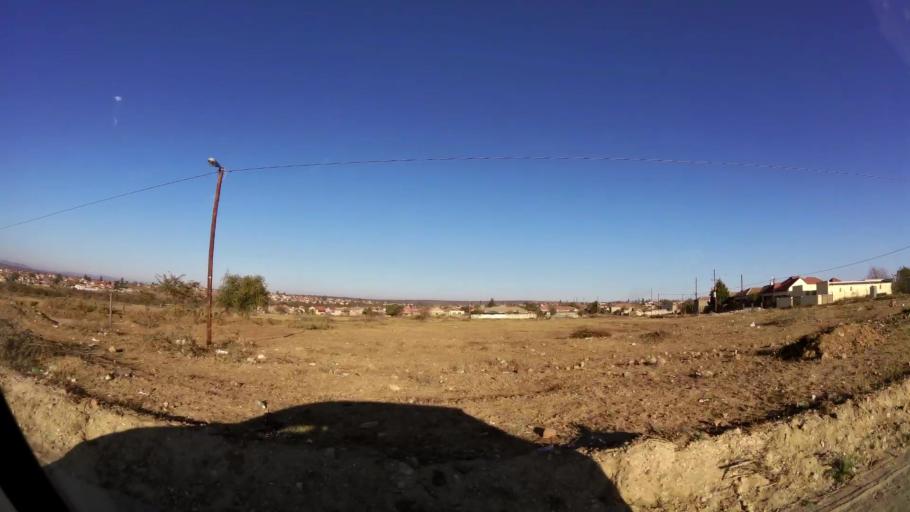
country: ZA
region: Limpopo
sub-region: Capricorn District Municipality
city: Polokwane
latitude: -23.8386
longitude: 29.3593
